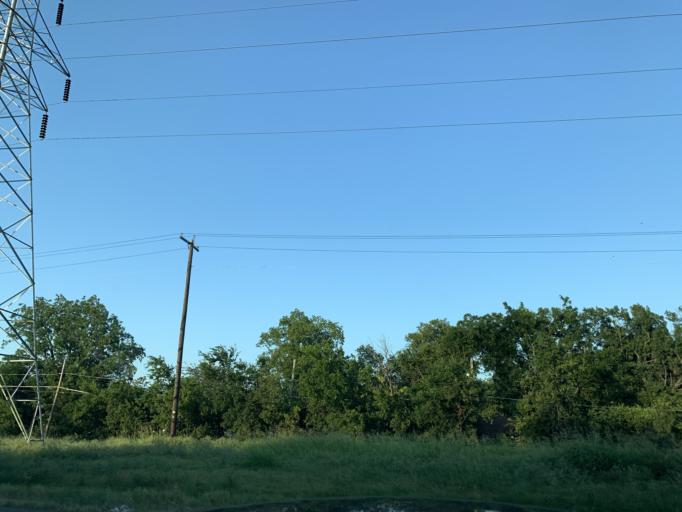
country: US
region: Texas
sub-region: Dallas County
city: Dallas
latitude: 32.7096
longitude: -96.8094
